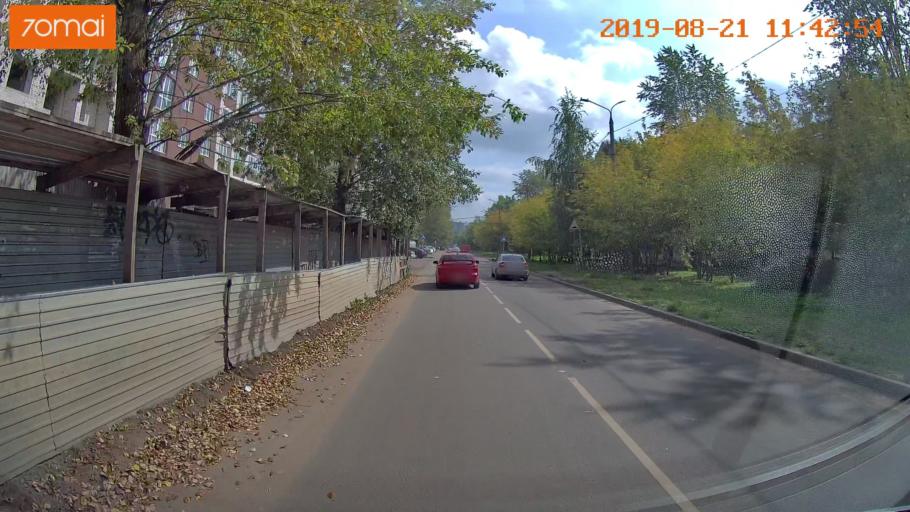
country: RU
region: Ivanovo
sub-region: Gorod Ivanovo
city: Ivanovo
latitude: 57.0015
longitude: 40.9538
